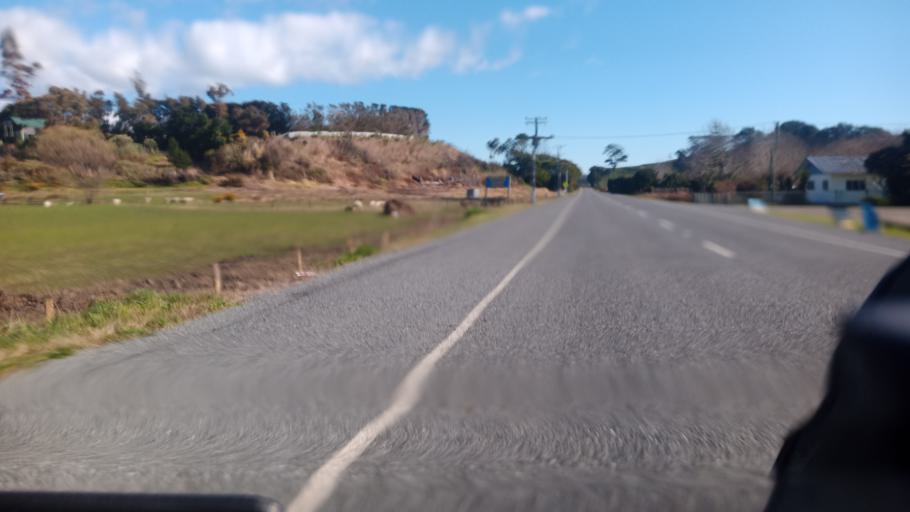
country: NZ
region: Bay of Plenty
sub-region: Opotiki District
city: Opotiki
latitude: -37.9888
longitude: 177.3529
